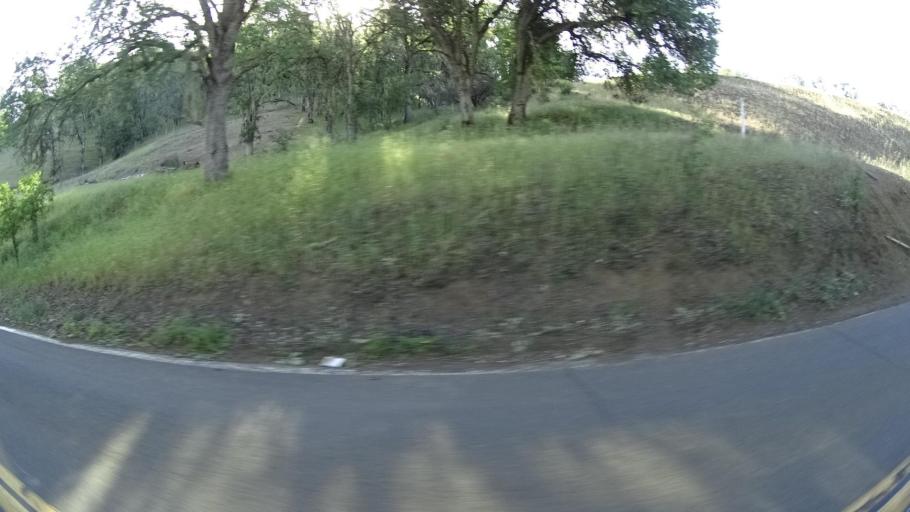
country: US
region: California
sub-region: Lake County
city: North Lakeport
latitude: 39.0990
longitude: -122.9685
